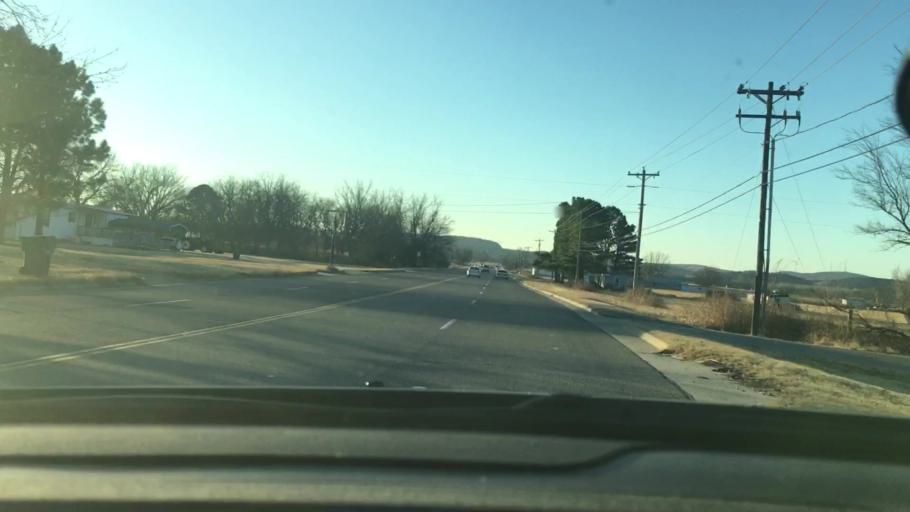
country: US
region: Oklahoma
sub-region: Murray County
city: Davis
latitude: 34.4742
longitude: -97.1318
